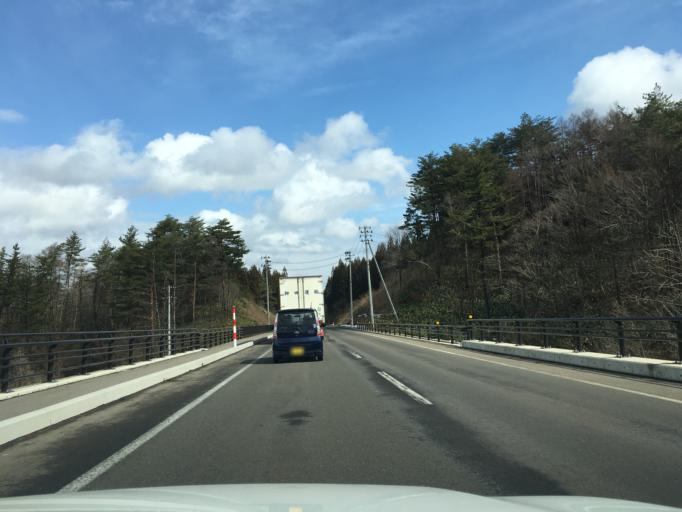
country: JP
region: Akita
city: Takanosu
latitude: 40.1071
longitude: 140.3533
